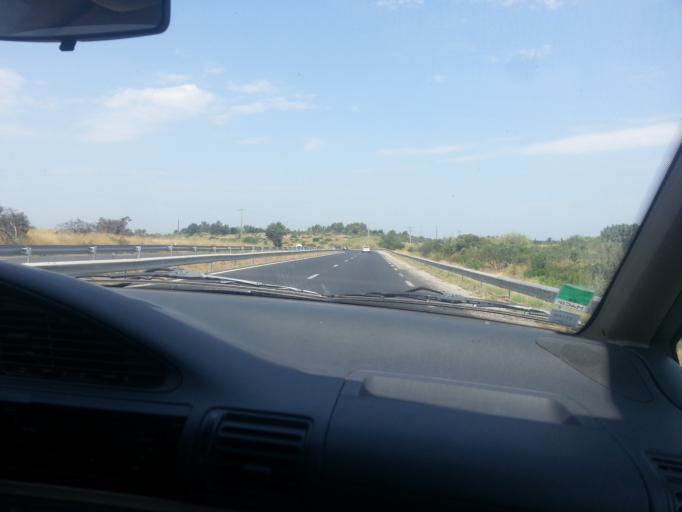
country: FR
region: Languedoc-Roussillon
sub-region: Departement de l'Herault
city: Grabels
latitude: 43.6274
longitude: 3.7833
